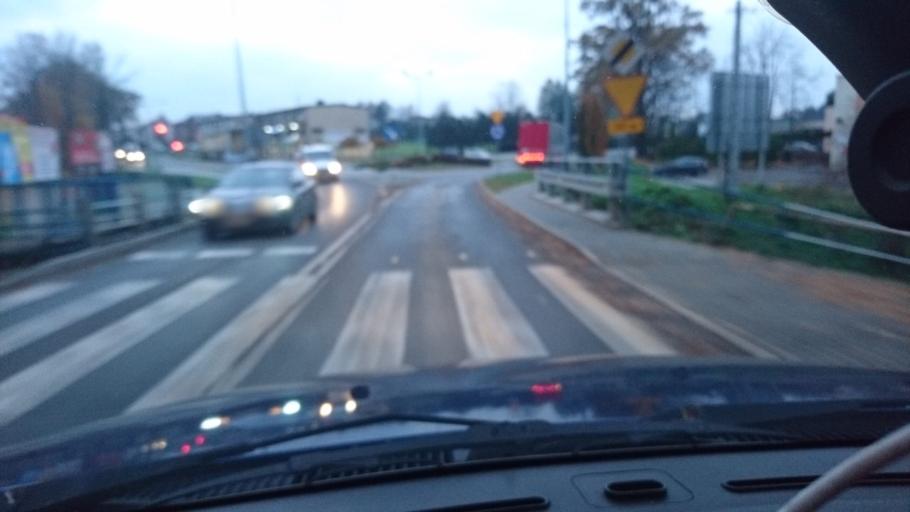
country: PL
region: Silesian Voivodeship
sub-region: Powiat bielski
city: Bestwina
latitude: 49.8972
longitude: 19.0589
